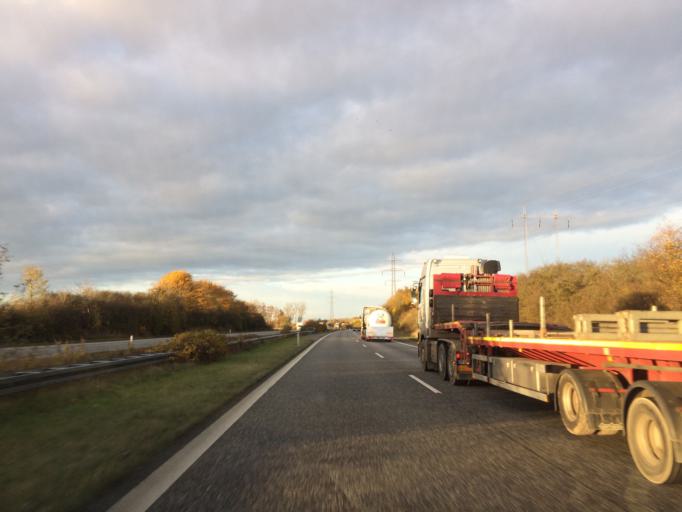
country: DK
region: South Denmark
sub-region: Aabenraa Kommune
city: Rodekro
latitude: 55.0448
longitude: 9.3526
